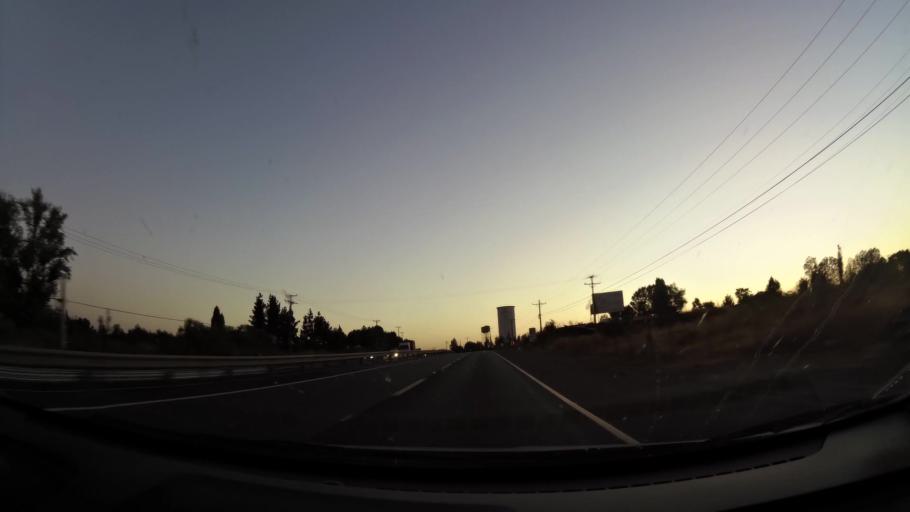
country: CL
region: Maule
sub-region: Provincia de Linares
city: Parral
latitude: -36.0909
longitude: -71.7943
